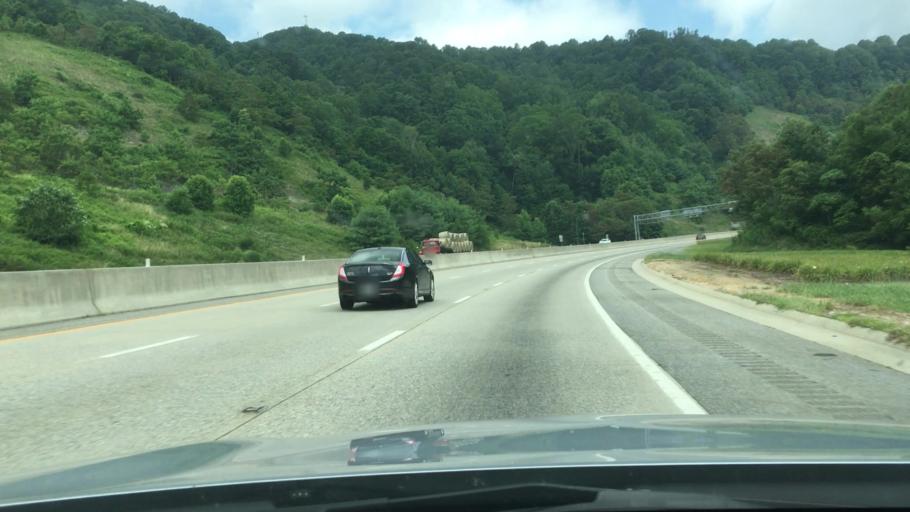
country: US
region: North Carolina
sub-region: Madison County
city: Mars Hill
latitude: 35.8803
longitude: -82.5494
